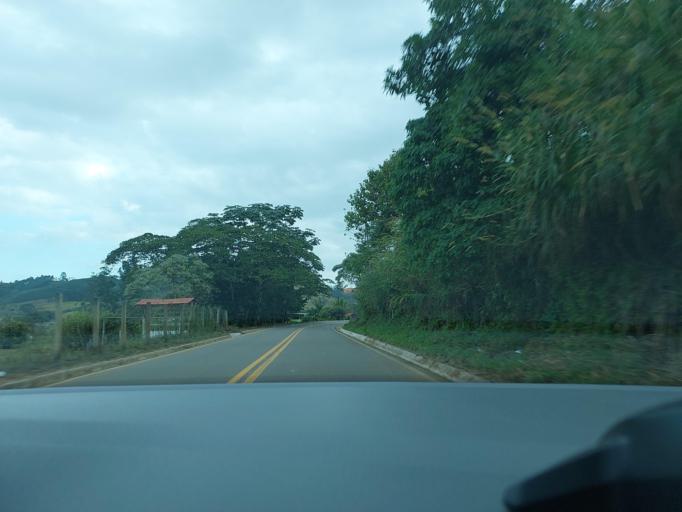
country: BR
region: Minas Gerais
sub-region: Mirai
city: Mirai
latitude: -21.0019
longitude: -42.5508
